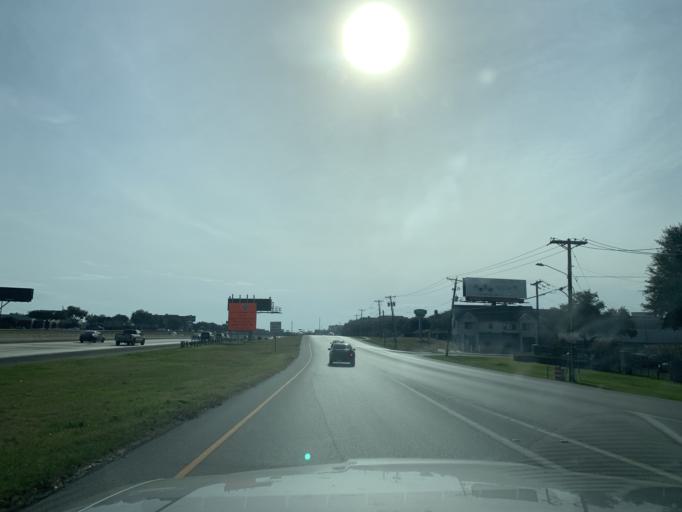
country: US
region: Texas
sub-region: Tarrant County
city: Euless
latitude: 32.7903
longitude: -97.0583
